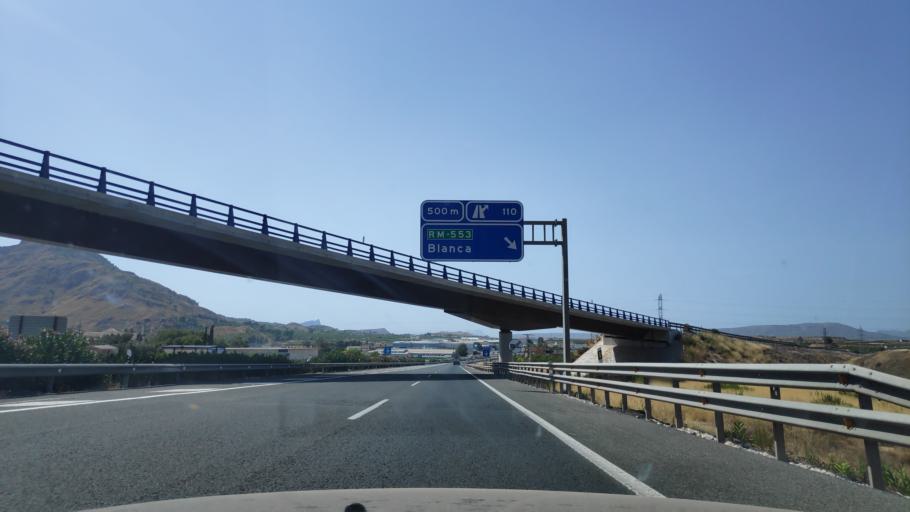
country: ES
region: Murcia
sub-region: Murcia
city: Ojos
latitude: 38.1863
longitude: -1.3236
